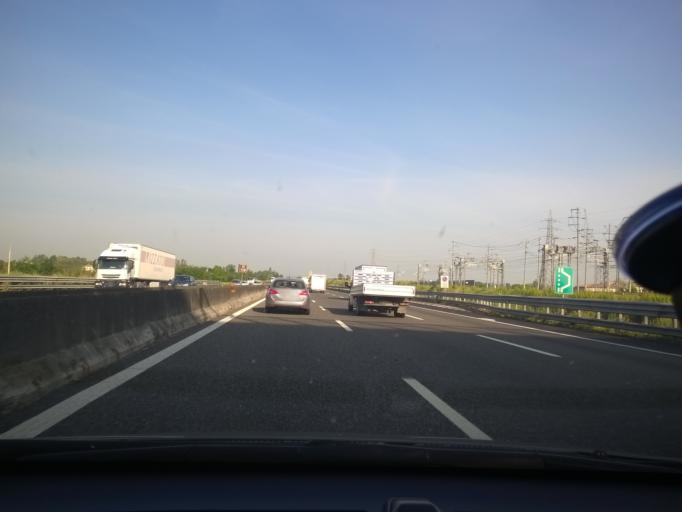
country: IT
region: Emilia-Romagna
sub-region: Provincia di Parma
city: Sorbolo
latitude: 44.8089
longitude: 10.4271
